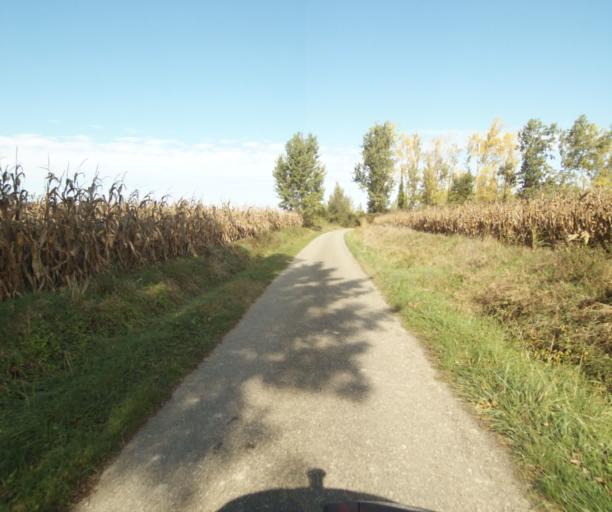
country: FR
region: Midi-Pyrenees
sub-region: Departement du Tarn-et-Garonne
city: Finhan
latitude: 43.9080
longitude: 1.2152
